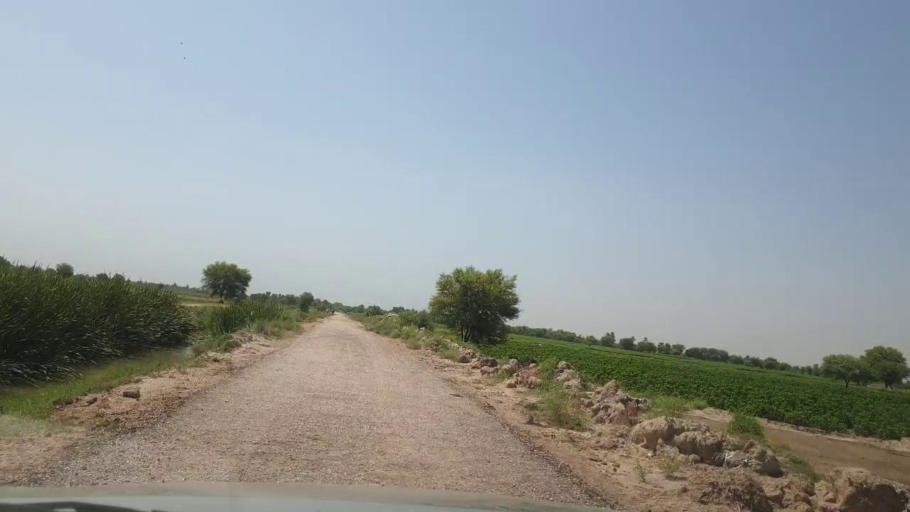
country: PK
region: Sindh
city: Rohri
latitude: 27.6630
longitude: 68.9809
